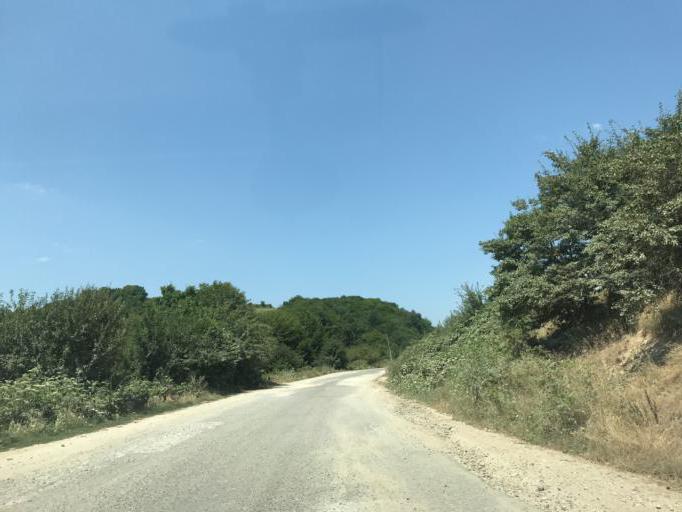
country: AZ
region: Tartar Rayon
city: Martakert
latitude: 40.1041
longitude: 46.6607
